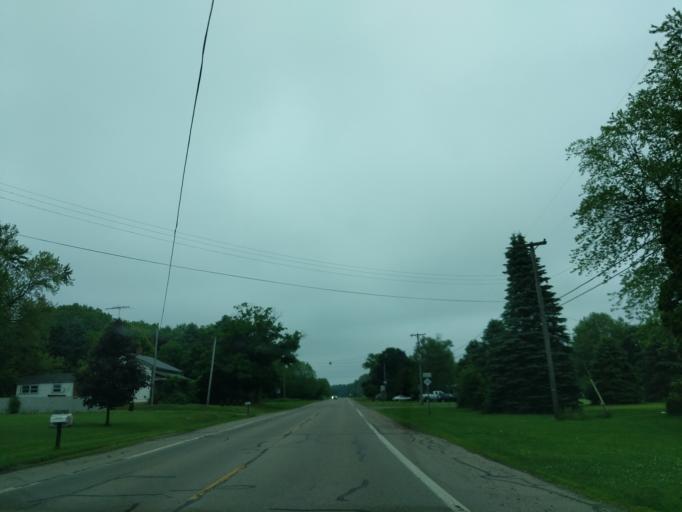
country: US
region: Michigan
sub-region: Hillsdale County
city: Litchfield
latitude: 42.0398
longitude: -84.7486
